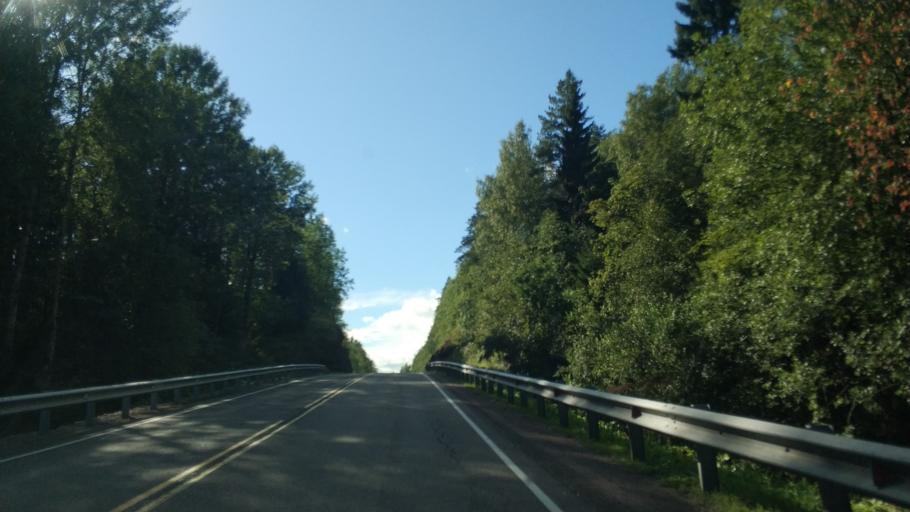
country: RU
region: Republic of Karelia
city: Khelyulya
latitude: 61.6557
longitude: 30.6250
